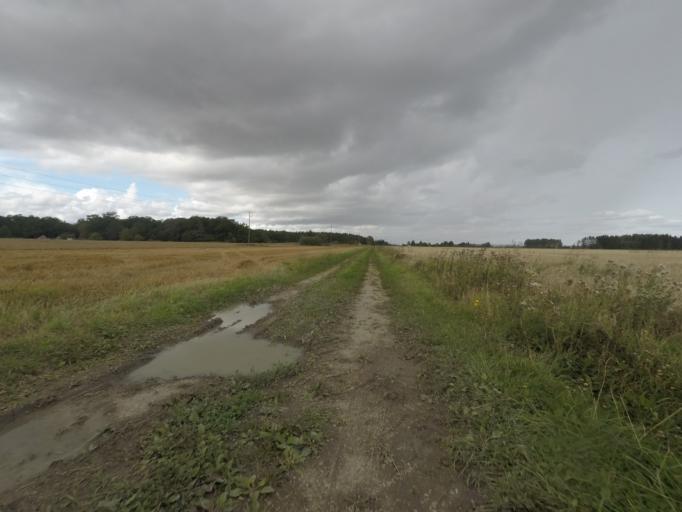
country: SE
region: Vaestmanland
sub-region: Kungsors Kommun
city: Kungsoer
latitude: 59.4604
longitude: 16.0471
